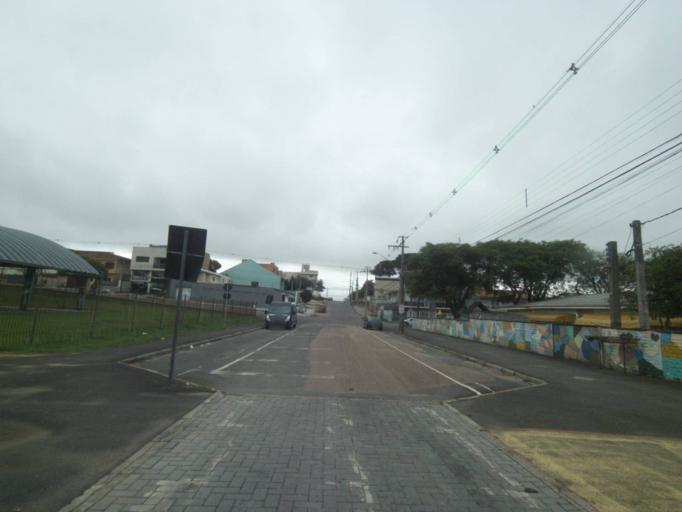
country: BR
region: Parana
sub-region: Sao Jose Dos Pinhais
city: Sao Jose dos Pinhais
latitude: -25.5450
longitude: -49.2838
